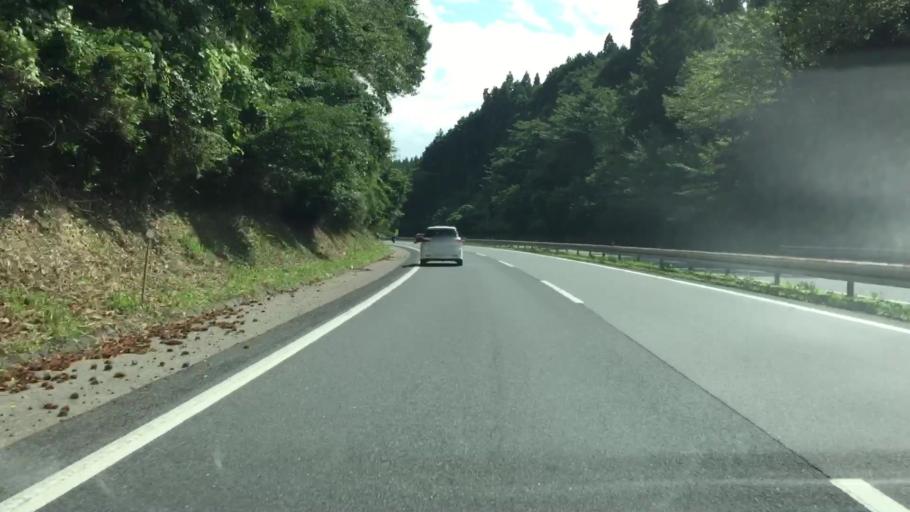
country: JP
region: Tochigi
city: Imaichi
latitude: 36.7159
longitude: 139.6774
